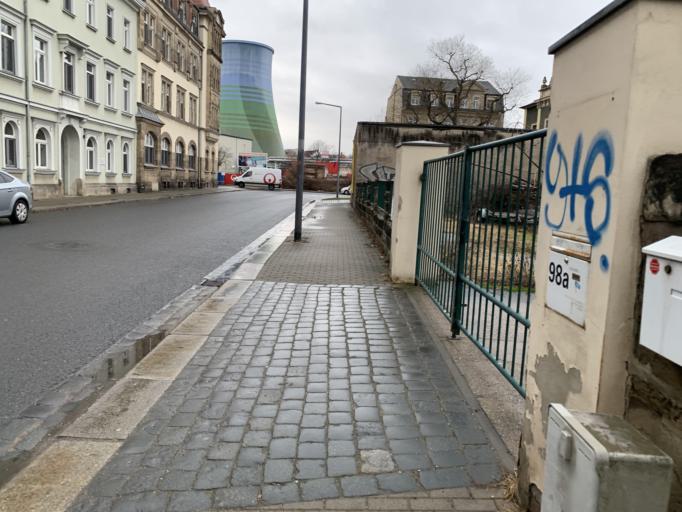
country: DE
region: Saxony
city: Dresden
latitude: 51.0456
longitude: 13.7142
